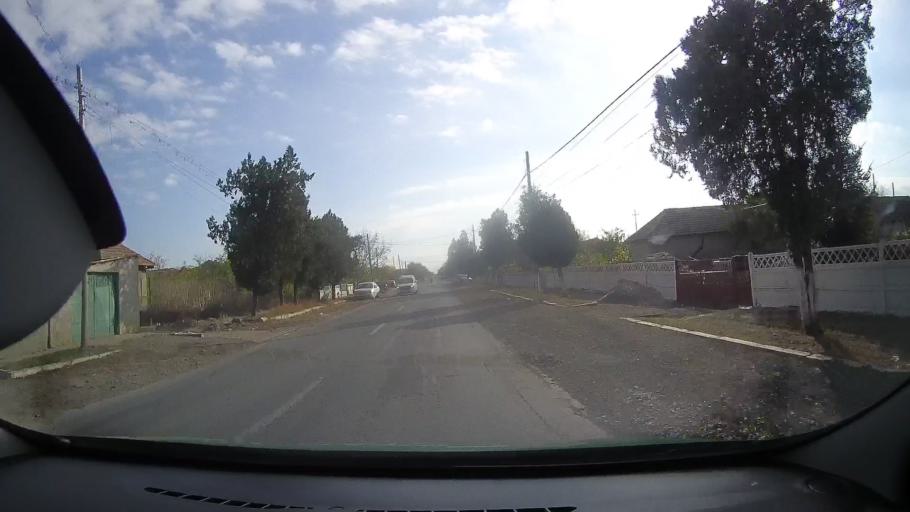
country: RO
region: Constanta
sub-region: Comuna Corbu
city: Corbu
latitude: 44.3936
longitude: 28.6619
